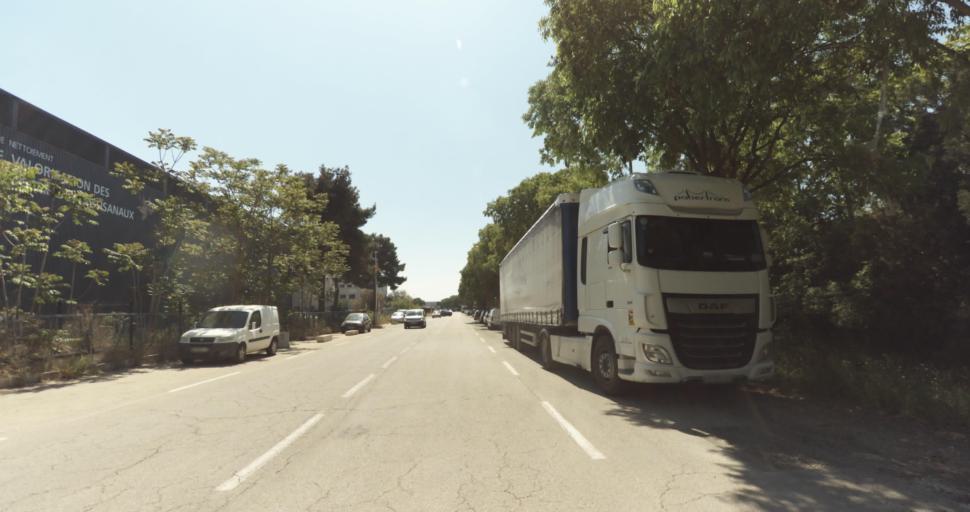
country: FR
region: Languedoc-Roussillon
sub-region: Departement du Gard
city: Milhaud
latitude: 43.8087
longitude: 4.3112
